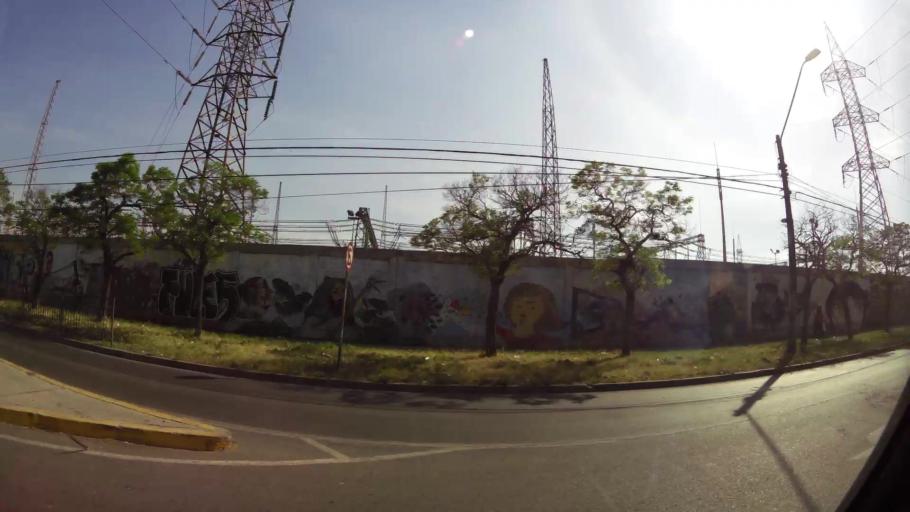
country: CL
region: Santiago Metropolitan
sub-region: Provincia de Santiago
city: Lo Prado
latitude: -33.4235
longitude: -70.7300
